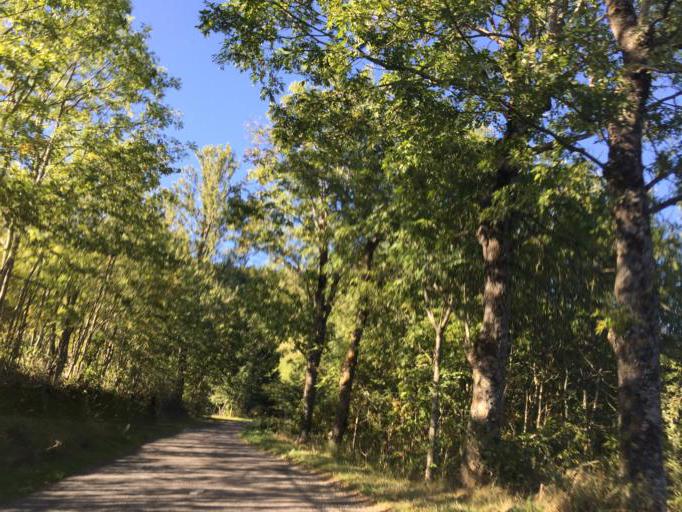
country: FR
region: Rhone-Alpes
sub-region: Departement de la Loire
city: Saint-Paul-en-Jarez
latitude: 45.4287
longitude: 4.5769
